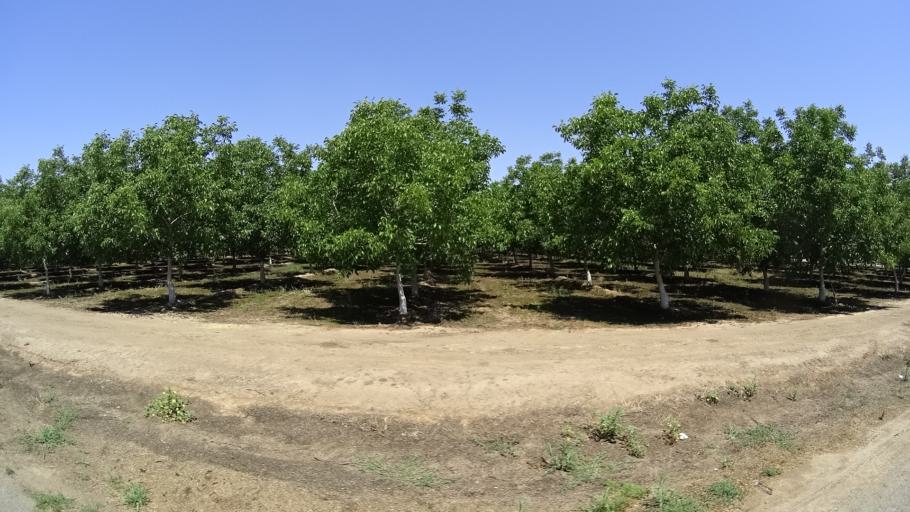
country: US
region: California
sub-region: Kings County
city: Lucerne
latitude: 36.3572
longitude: -119.6838
